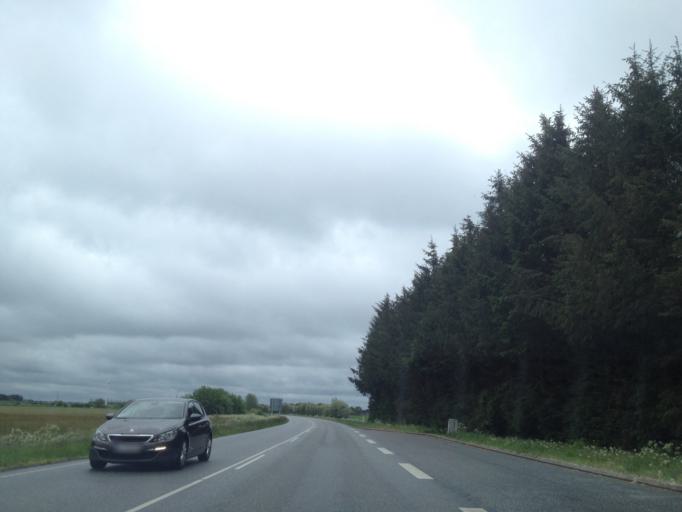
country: DK
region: South Denmark
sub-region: Tonder Kommune
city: Tonder
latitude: 54.9648
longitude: 8.8691
